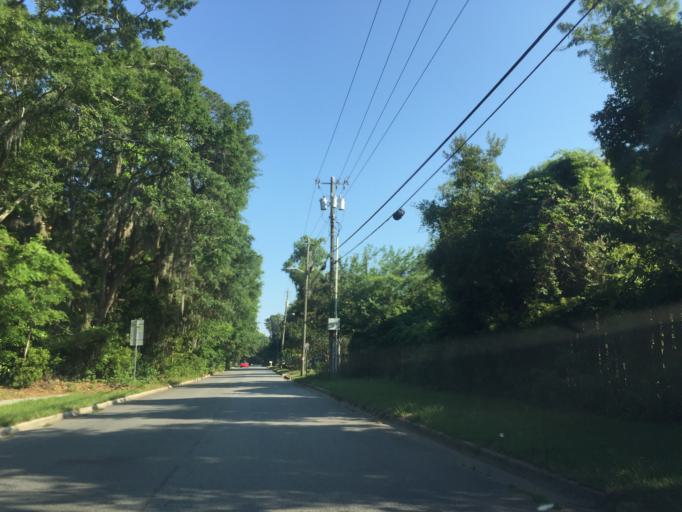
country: US
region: Georgia
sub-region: Chatham County
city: Isle of Hope
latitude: 31.9933
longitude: -81.0769
